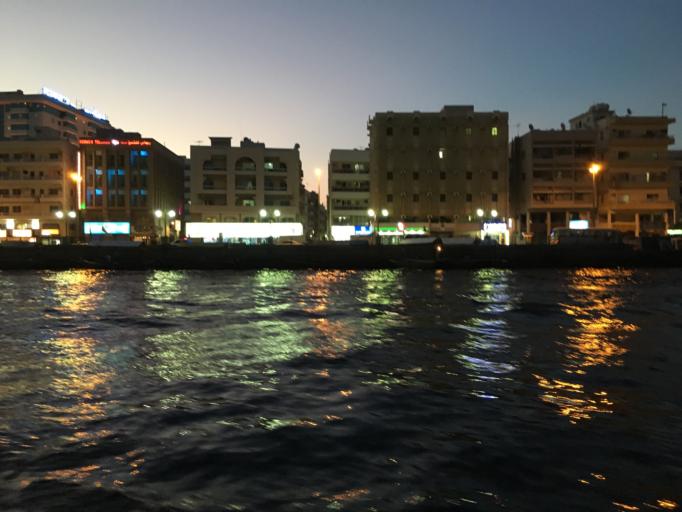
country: AE
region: Ash Shariqah
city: Sharjah
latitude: 25.2656
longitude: 55.2961
